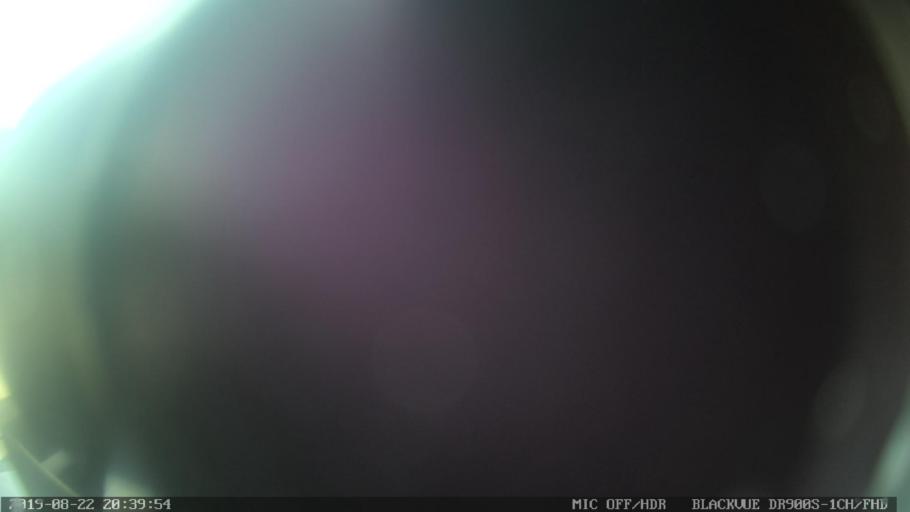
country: PT
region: Castelo Branco
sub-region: Proenca-A-Nova
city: Proenca-a-Nova
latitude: 39.6879
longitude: -7.7791
